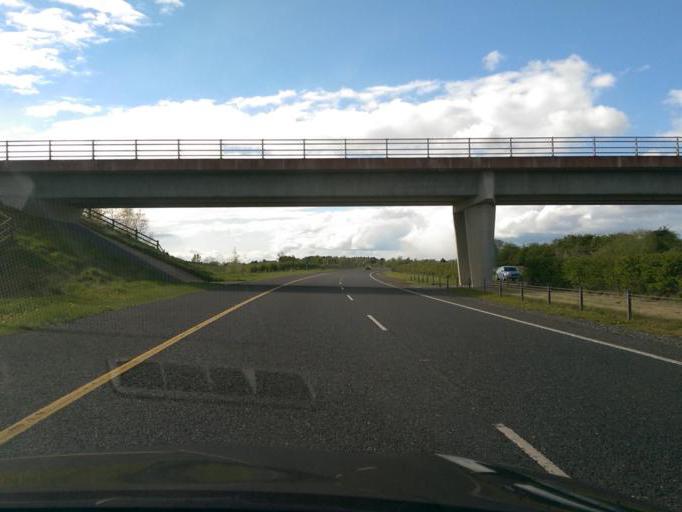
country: IE
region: Leinster
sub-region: An Mhi
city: Longwood
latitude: 53.4128
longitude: -6.8984
